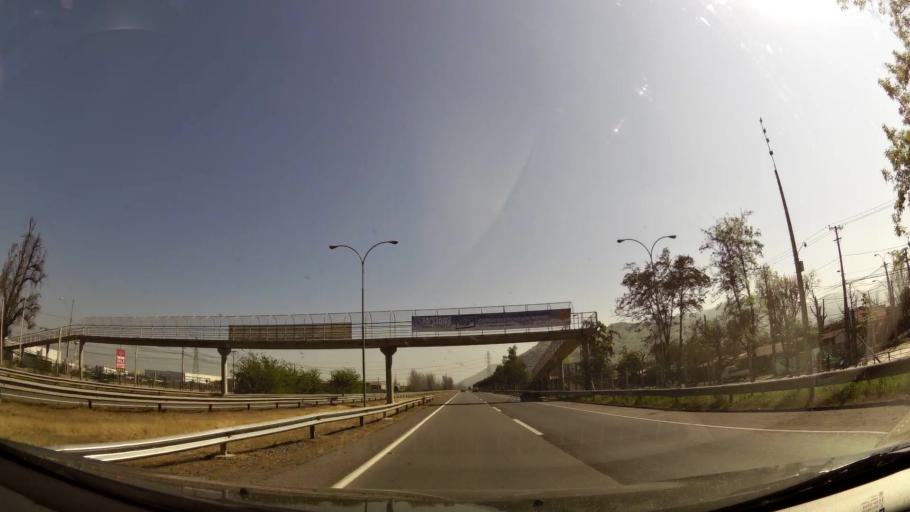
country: CL
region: Santiago Metropolitan
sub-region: Provincia de Chacabuco
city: Chicureo Abajo
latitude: -33.3600
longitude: -70.6907
